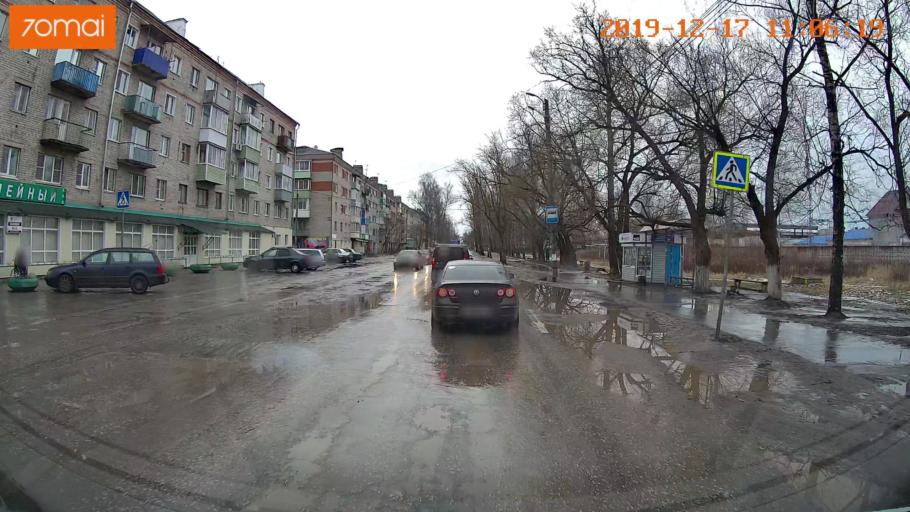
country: RU
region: Vladimir
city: Gus'-Khrustal'nyy
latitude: 55.6161
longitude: 40.6446
